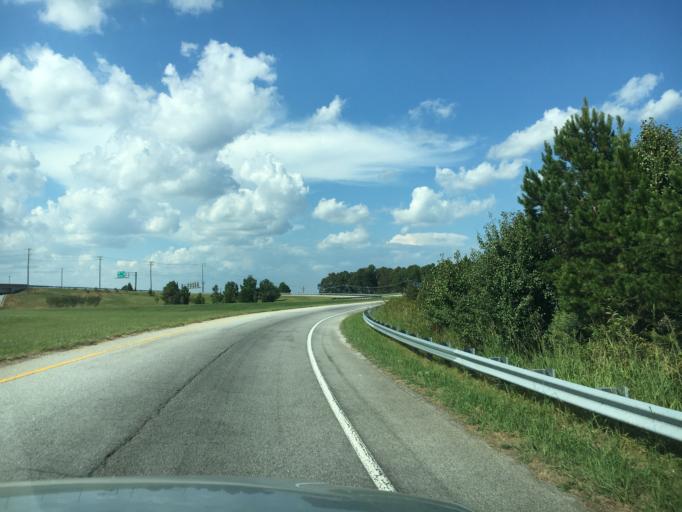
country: US
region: South Carolina
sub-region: Greenville County
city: Simpsonville
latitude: 34.7176
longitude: -82.2531
